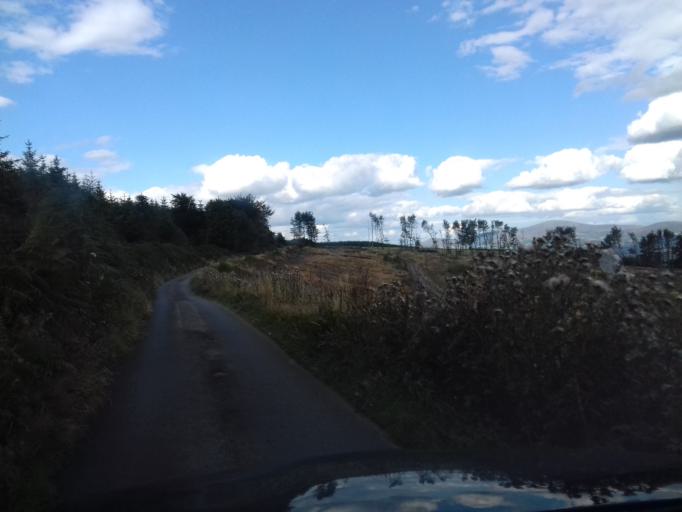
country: IE
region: Leinster
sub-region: Kilkenny
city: Graiguenamanagh
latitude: 52.5578
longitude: -7.0150
